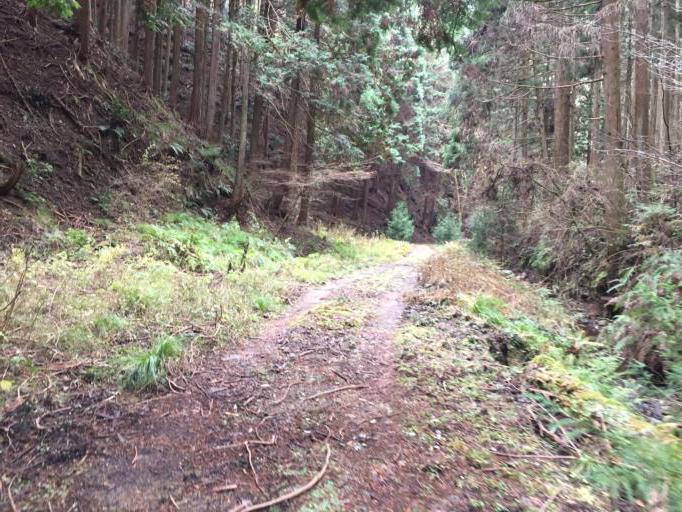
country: JP
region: Kyoto
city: Kameoka
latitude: 34.9786
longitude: 135.6170
